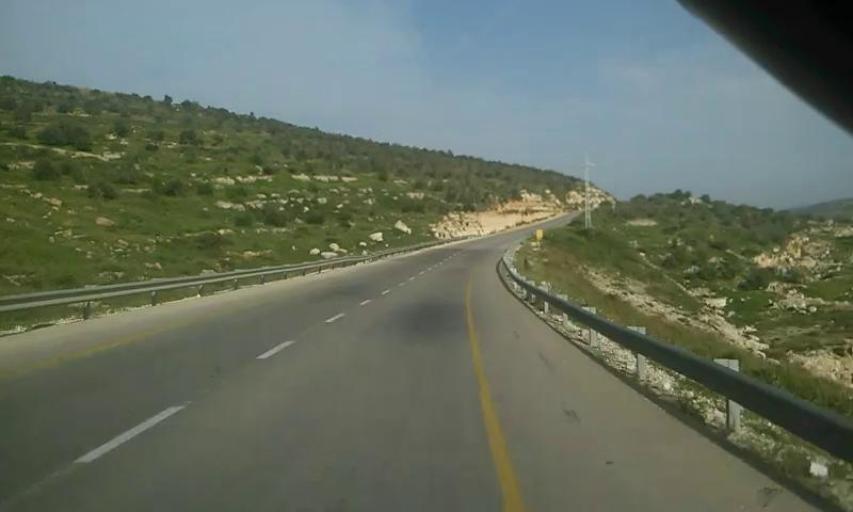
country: PS
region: West Bank
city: Till
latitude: 32.1913
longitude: 35.2023
